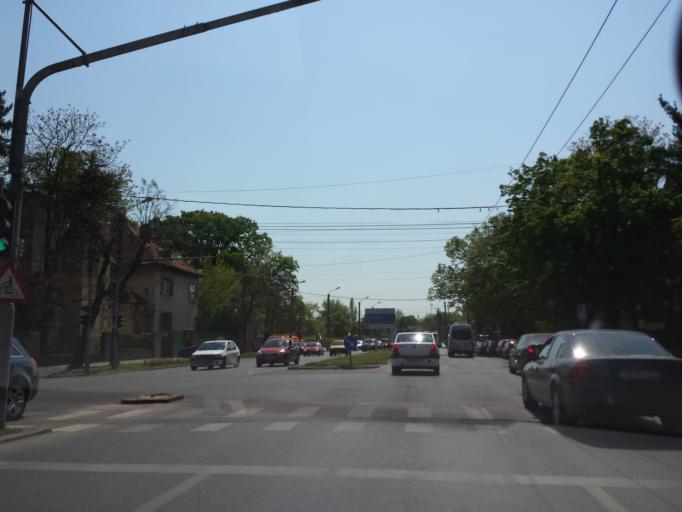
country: RO
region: Timis
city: Timisoara
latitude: 45.7520
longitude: 21.2332
